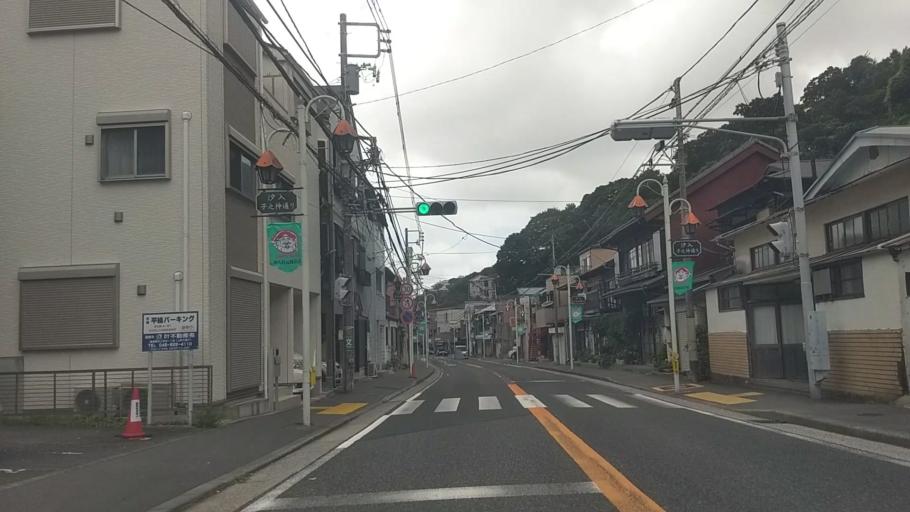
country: JP
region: Kanagawa
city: Yokosuka
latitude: 35.2767
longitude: 139.6601
